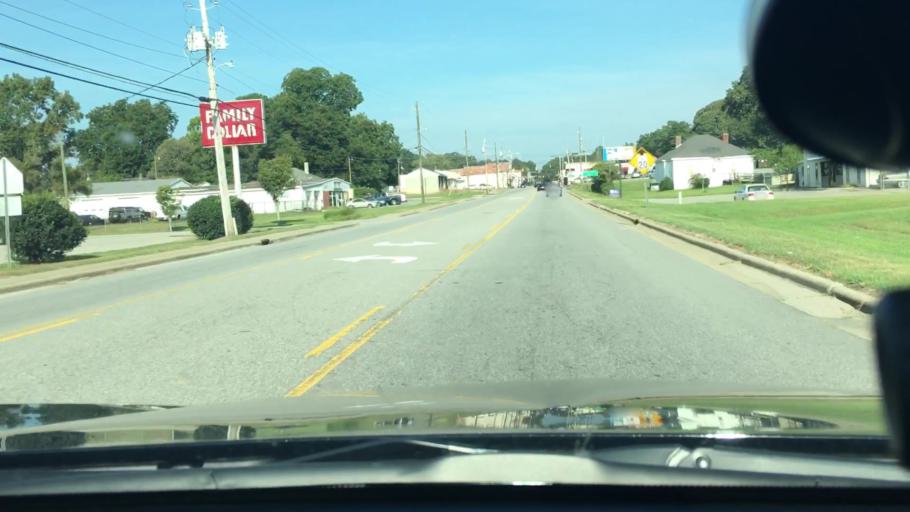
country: US
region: North Carolina
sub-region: Edgecombe County
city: Pinetops
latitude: 35.7897
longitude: -77.6338
